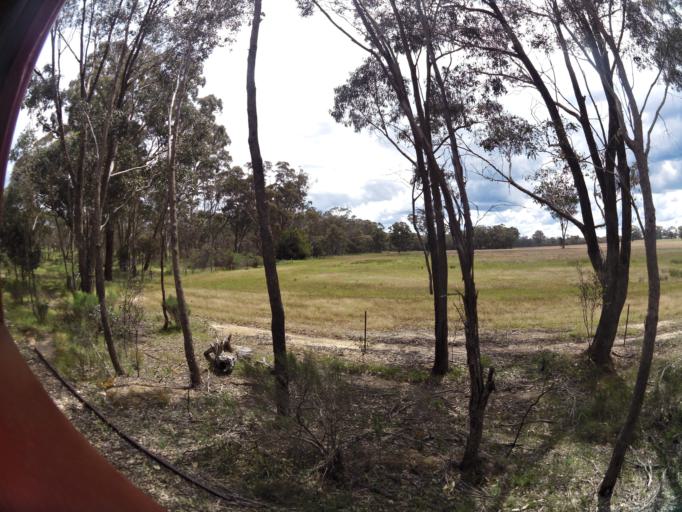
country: AU
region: Victoria
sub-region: Mount Alexander
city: Castlemaine
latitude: -36.9930
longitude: 144.0943
